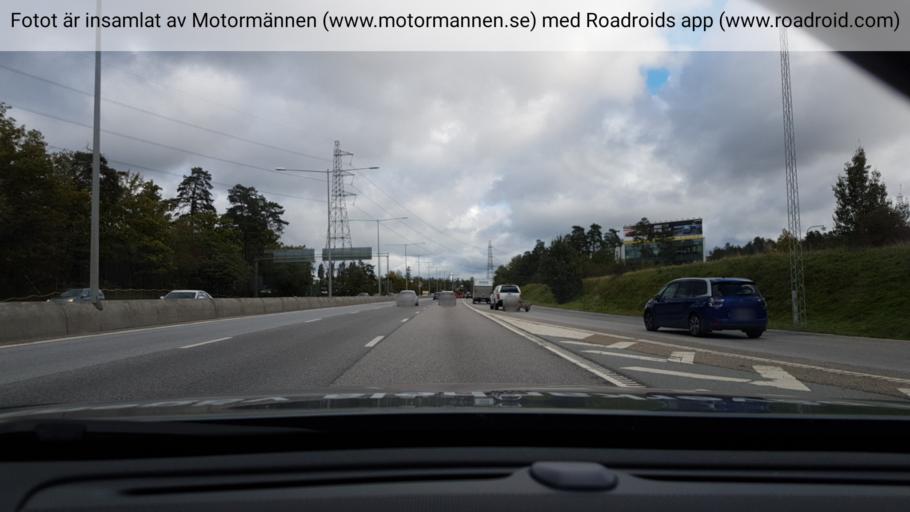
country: SE
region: Stockholm
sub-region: Huddinge Kommun
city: Segeltorp
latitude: 59.2785
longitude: 17.9165
